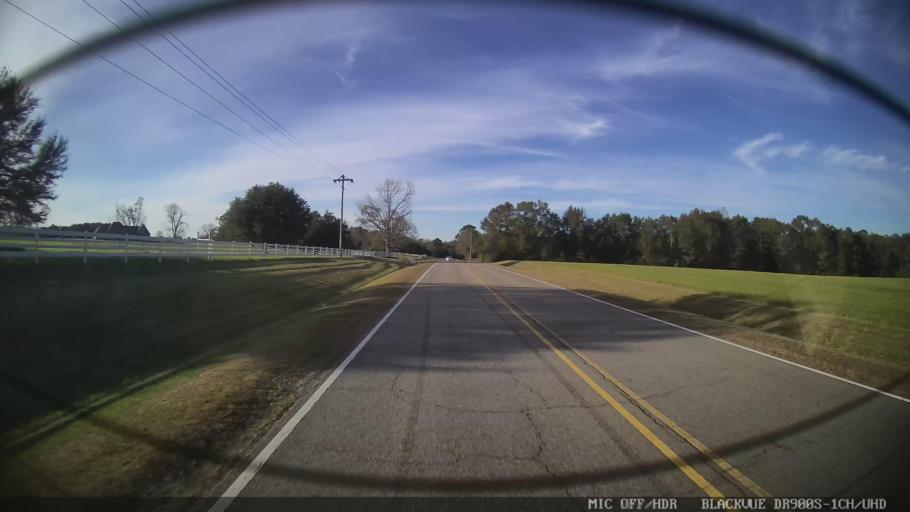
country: US
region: Mississippi
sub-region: Lamar County
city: Purvis
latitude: 31.1957
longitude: -89.2896
